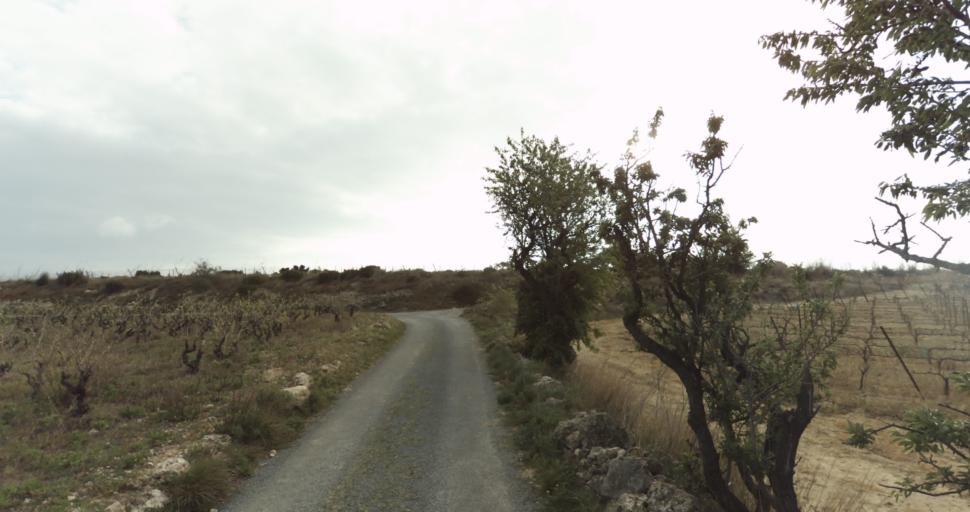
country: FR
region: Languedoc-Roussillon
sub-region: Departement de l'Aude
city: Leucate
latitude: 42.9290
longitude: 3.0254
